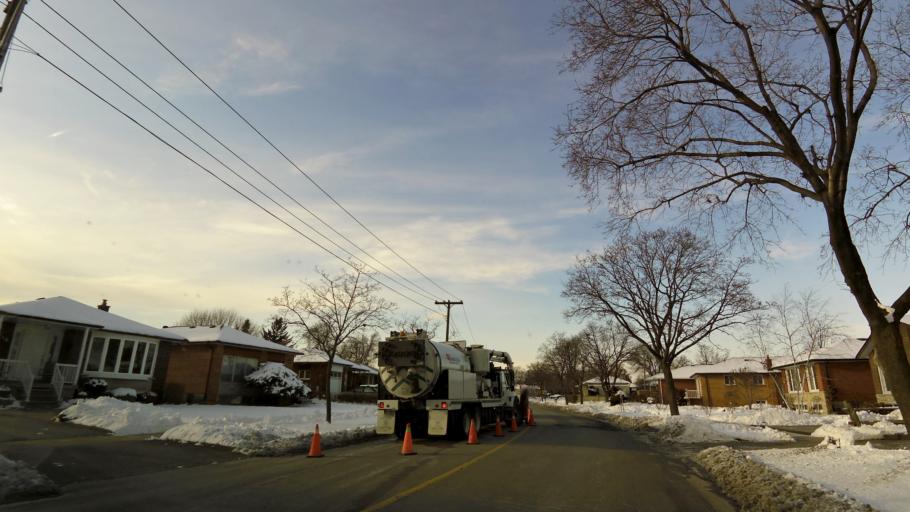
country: CA
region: Ontario
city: Etobicoke
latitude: 43.6579
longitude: -79.5779
